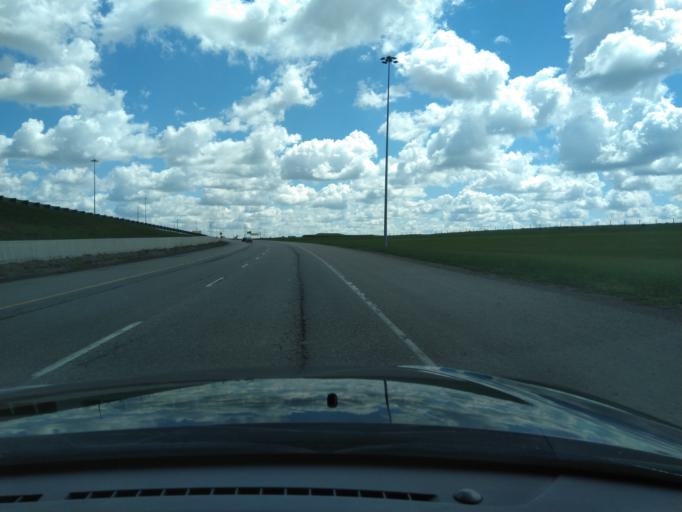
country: CA
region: Alberta
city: Airdrie
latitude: 51.1744
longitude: -113.9971
